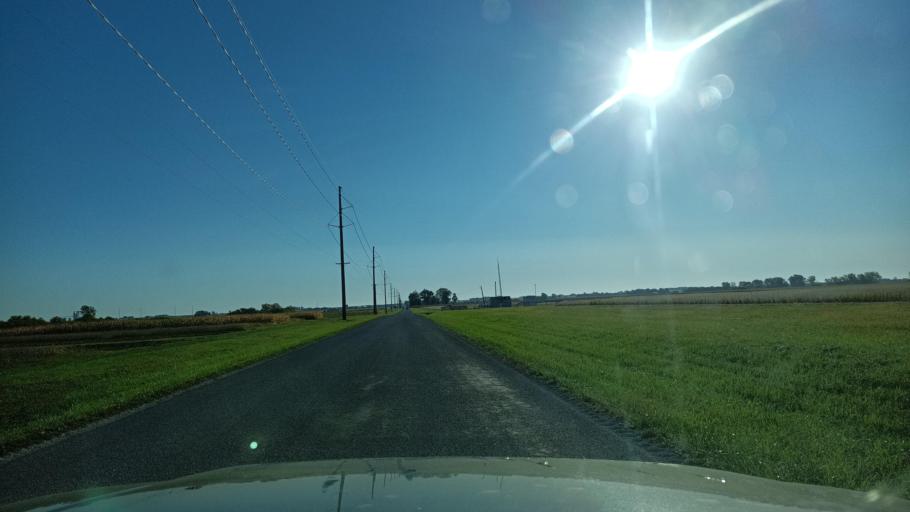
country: US
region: Illinois
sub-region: Champaign County
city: Savoy
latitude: 40.0543
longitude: -88.2370
